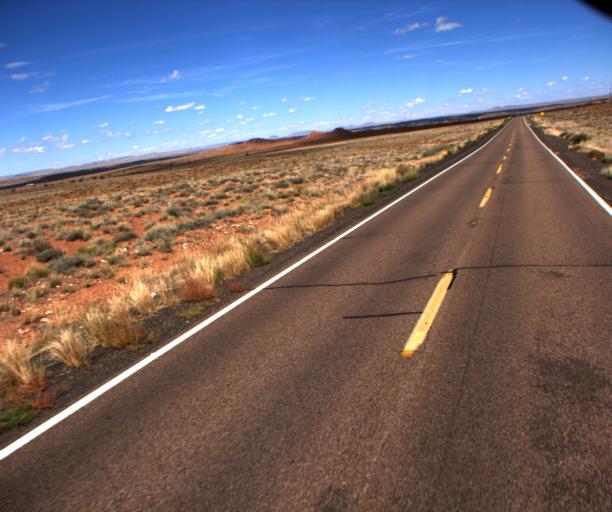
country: US
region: Arizona
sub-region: Navajo County
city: Holbrook
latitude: 34.8398
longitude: -110.1816
